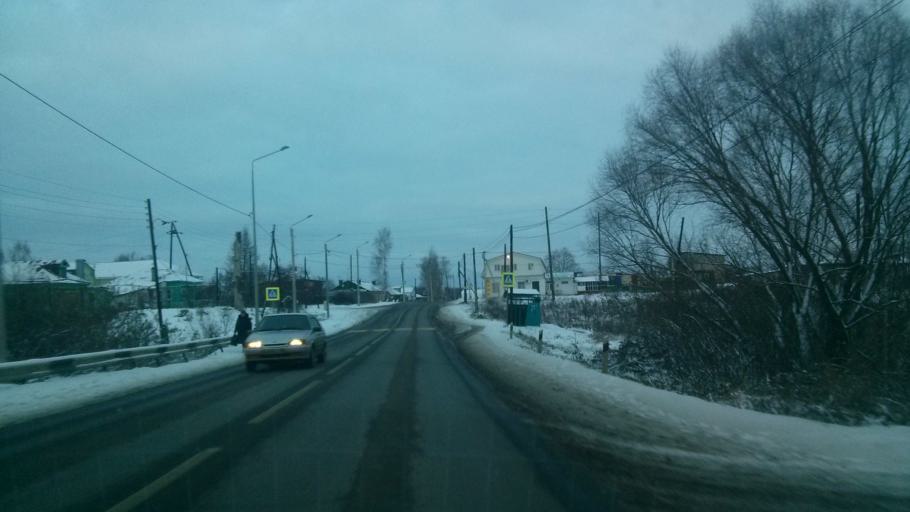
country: RU
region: Nizjnij Novgorod
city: Vorsma
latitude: 56.0363
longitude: 43.3684
